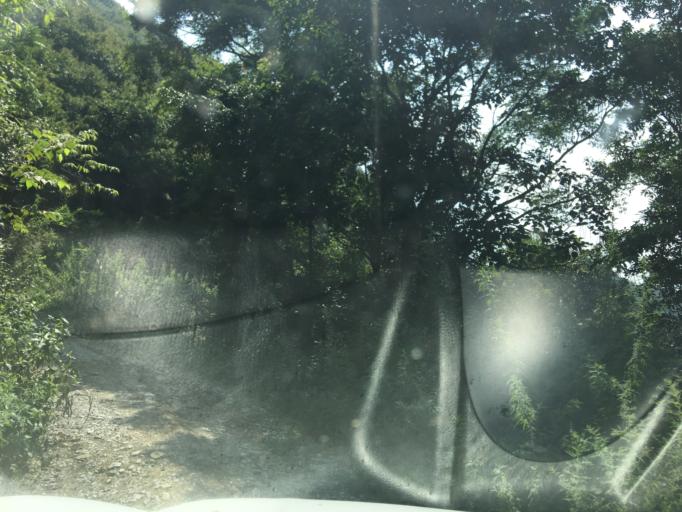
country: CN
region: Guangxi Zhuangzu Zizhiqu
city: Xinzhou
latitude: 24.9875
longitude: 105.7382
